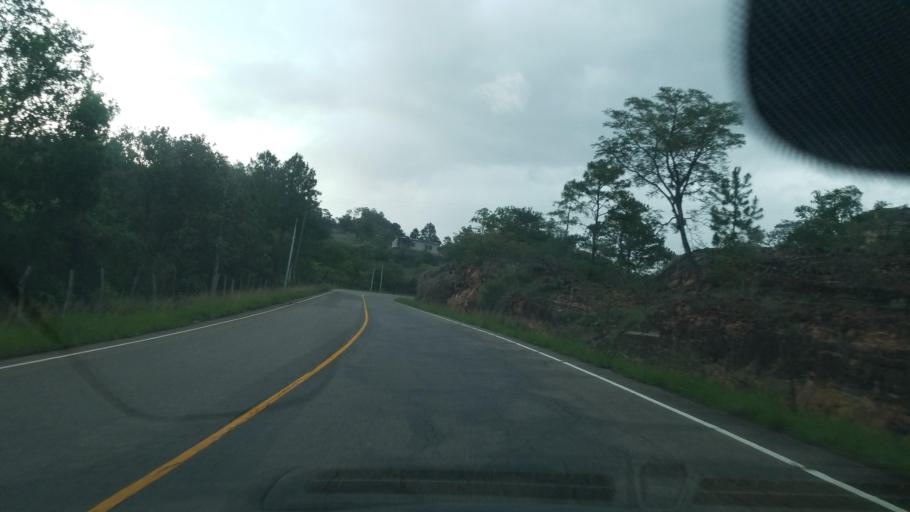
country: HN
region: Ocotepeque
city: Sinuapa
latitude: 14.5194
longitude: -89.2453
